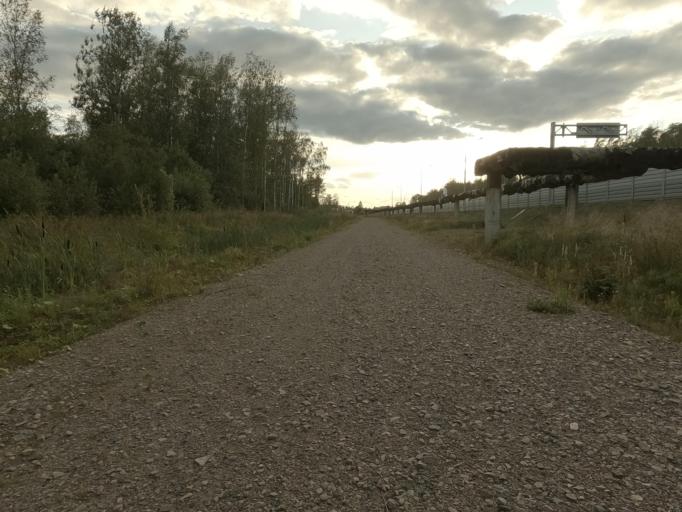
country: RU
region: Leningrad
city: Mga
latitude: 59.7572
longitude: 31.0887
